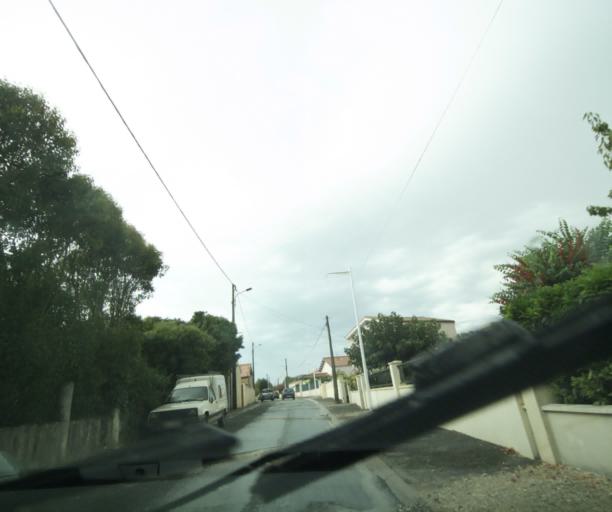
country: FR
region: Poitou-Charentes
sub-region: Departement de la Charente-Maritime
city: Tonnay-Charente
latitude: 45.9491
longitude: -0.8796
